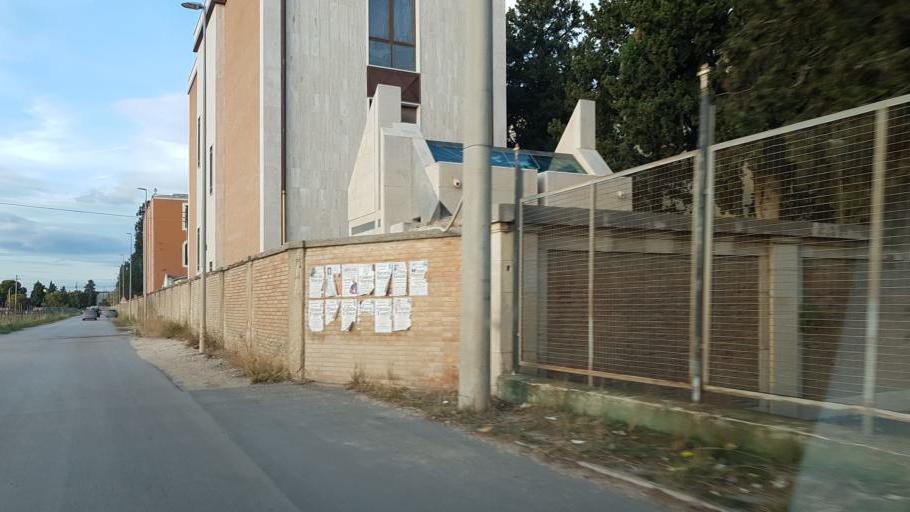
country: IT
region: Apulia
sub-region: Provincia di Foggia
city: Foggia
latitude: 41.4730
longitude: 15.5477
